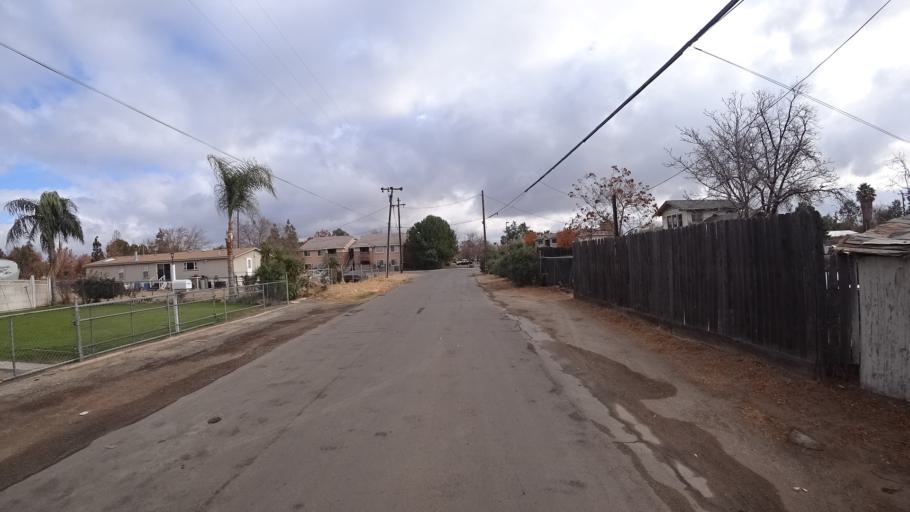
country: US
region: California
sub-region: Kern County
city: Bakersfield
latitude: 35.3368
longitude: -118.9906
